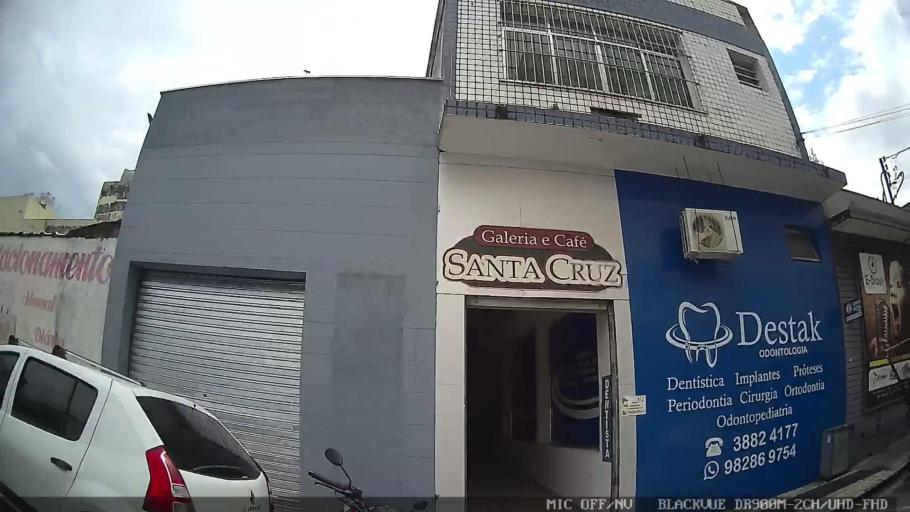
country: BR
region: Sao Paulo
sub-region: Caraguatatuba
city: Caraguatatuba
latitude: -23.6216
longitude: -45.4090
